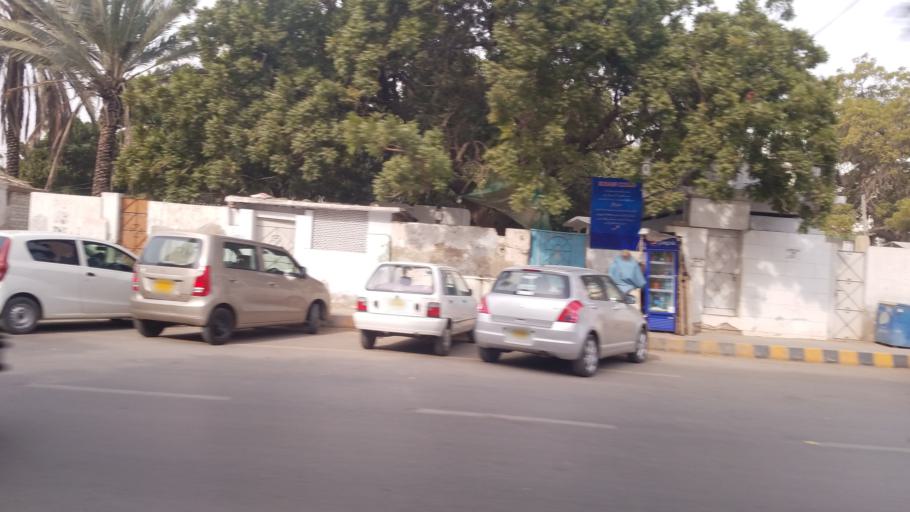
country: PK
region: Sindh
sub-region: Karachi District
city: Karachi
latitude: 24.8662
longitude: 67.0564
